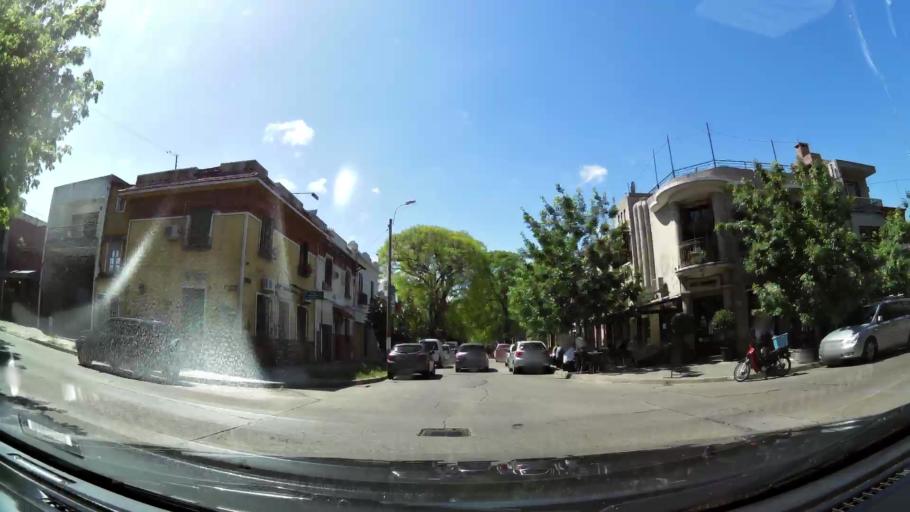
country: UY
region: Montevideo
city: Montevideo
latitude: -34.9163
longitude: -56.1560
